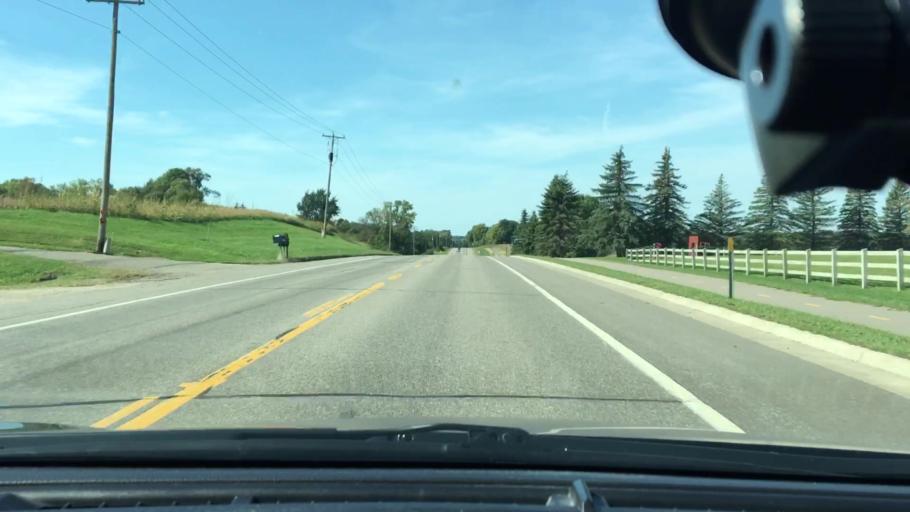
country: US
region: Minnesota
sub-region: Wright County
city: Hanover
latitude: 45.1525
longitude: -93.6481
